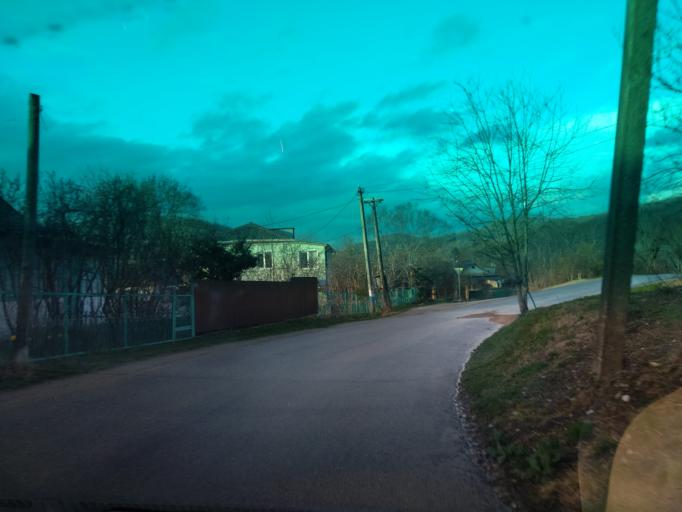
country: RU
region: Krasnodarskiy
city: Novomikhaylovskiy
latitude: 44.2703
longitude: 38.8306
